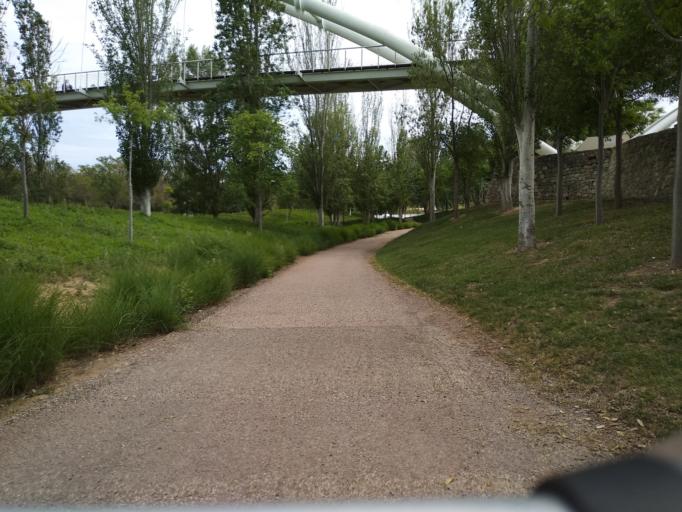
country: ES
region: Valencia
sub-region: Provincia de Valencia
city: Mislata
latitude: 39.4781
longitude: -0.4095
